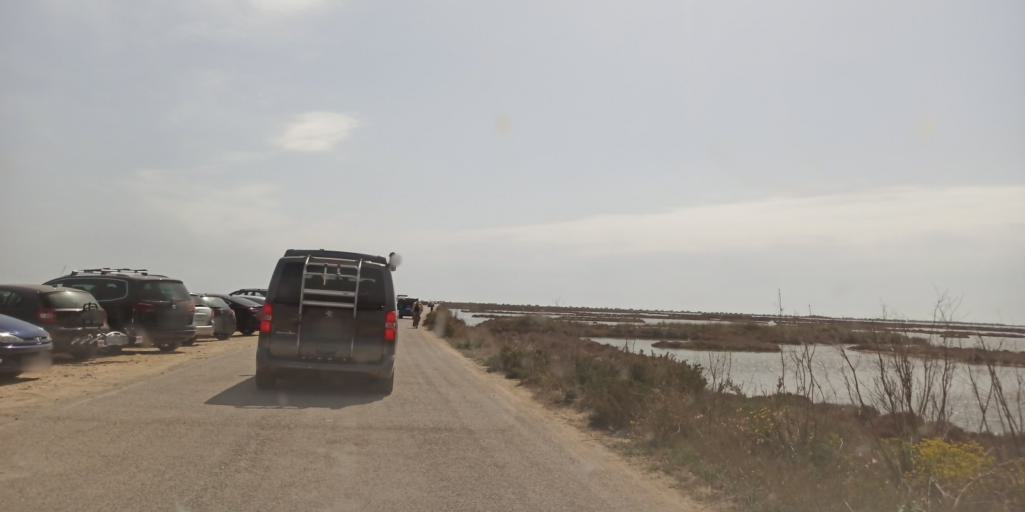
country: ES
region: Catalonia
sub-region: Provincia de Tarragona
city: Deltebre
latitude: 40.6422
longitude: 0.7371
